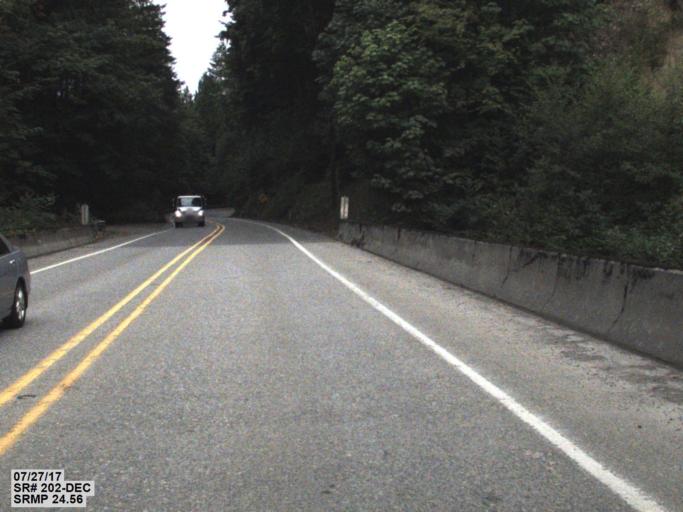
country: US
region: Washington
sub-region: King County
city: Snoqualmie
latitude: 47.5542
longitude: -121.8359
